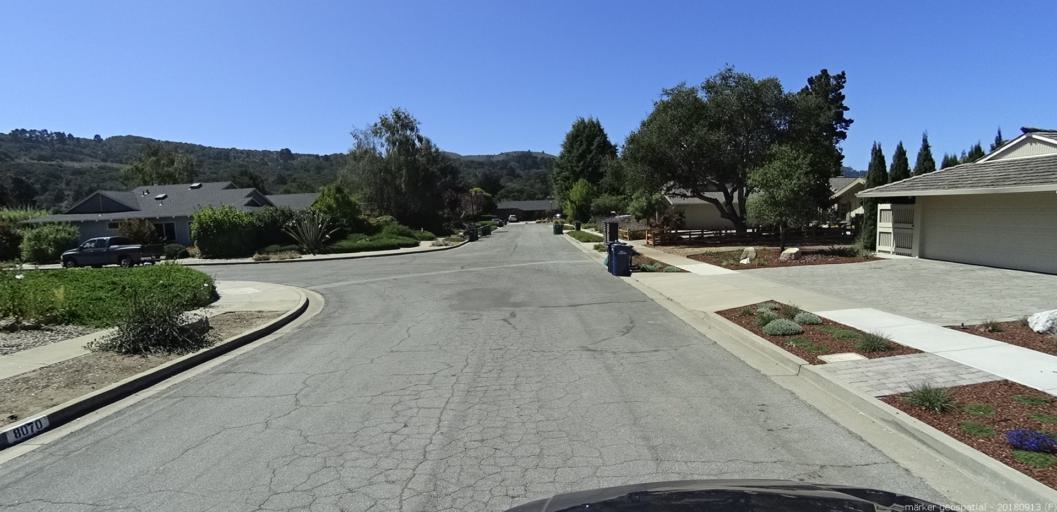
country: US
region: California
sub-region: Monterey County
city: Del Rey Oaks
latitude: 36.5322
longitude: -121.8547
